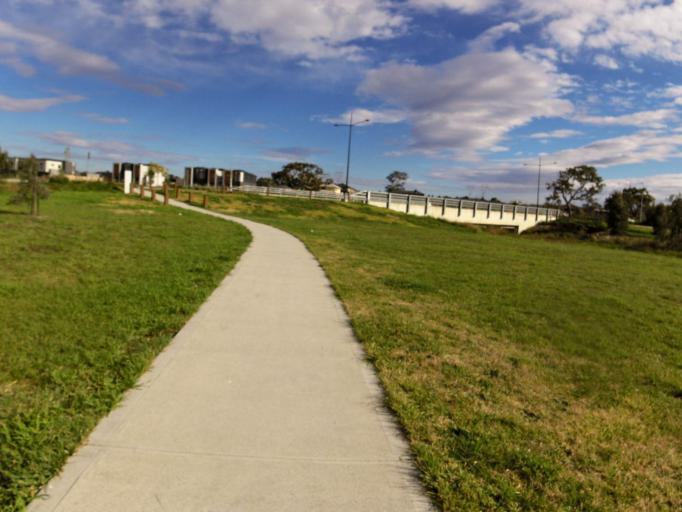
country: AU
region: Victoria
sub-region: Whittlesea
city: Epping
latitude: -37.6217
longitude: 145.0394
